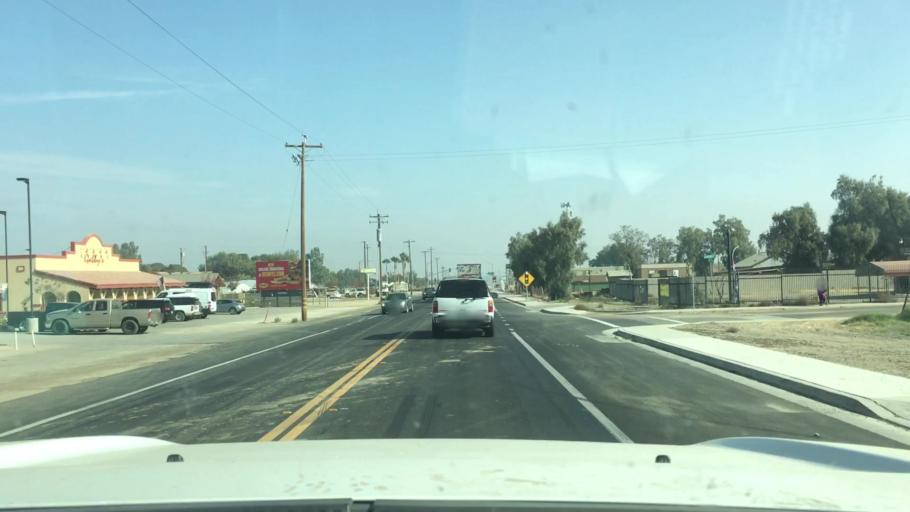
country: US
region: California
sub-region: Kern County
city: Lost Hills
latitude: 35.6161
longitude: -119.6932
